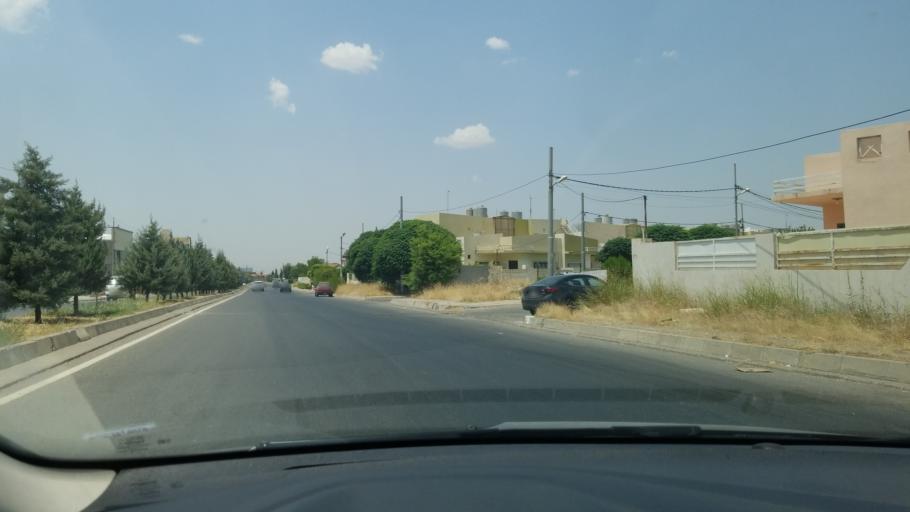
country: IQ
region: Arbil
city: Erbil
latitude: 36.1707
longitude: 44.0593
